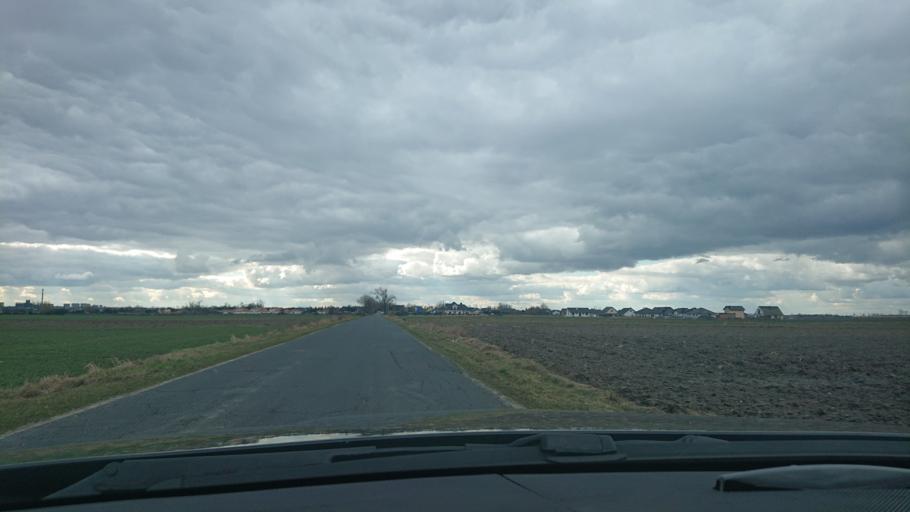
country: PL
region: Greater Poland Voivodeship
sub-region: Powiat gnieznienski
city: Gniezno
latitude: 52.5822
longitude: 17.6455
